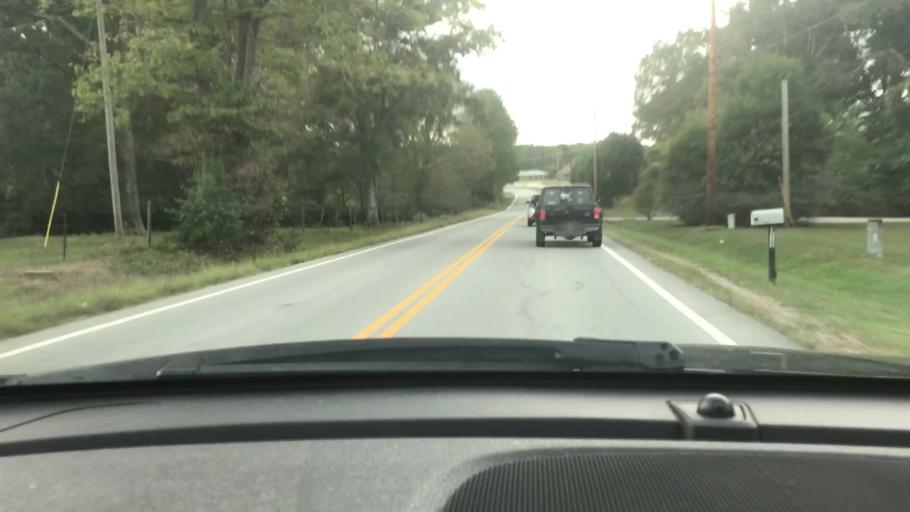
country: US
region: Tennessee
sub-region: Dickson County
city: Charlotte
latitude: 36.2124
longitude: -87.2655
